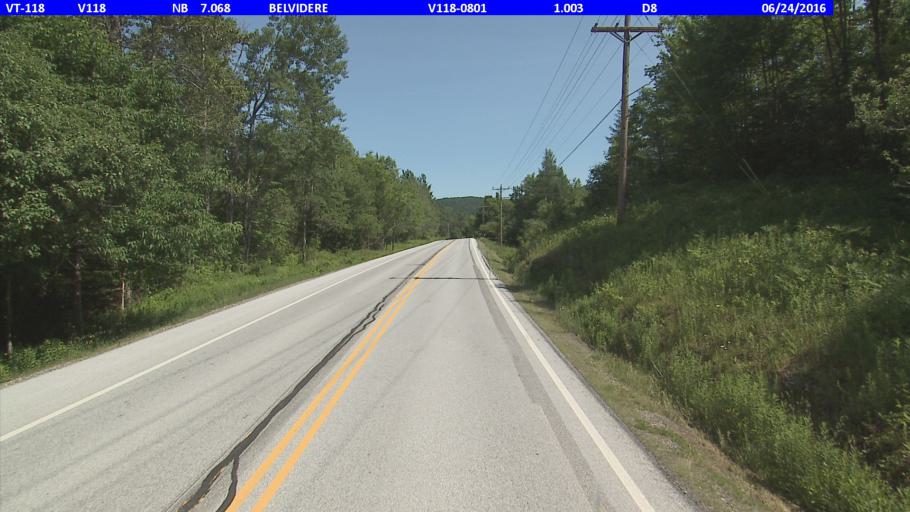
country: US
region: Vermont
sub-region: Lamoille County
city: Johnson
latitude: 44.7741
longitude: -72.6214
